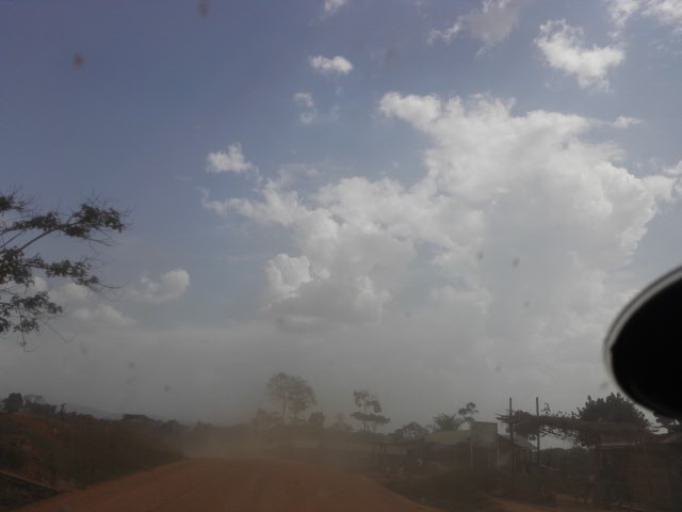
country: CD
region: Nord Kivu
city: Beni
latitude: 0.9829
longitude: 29.5871
